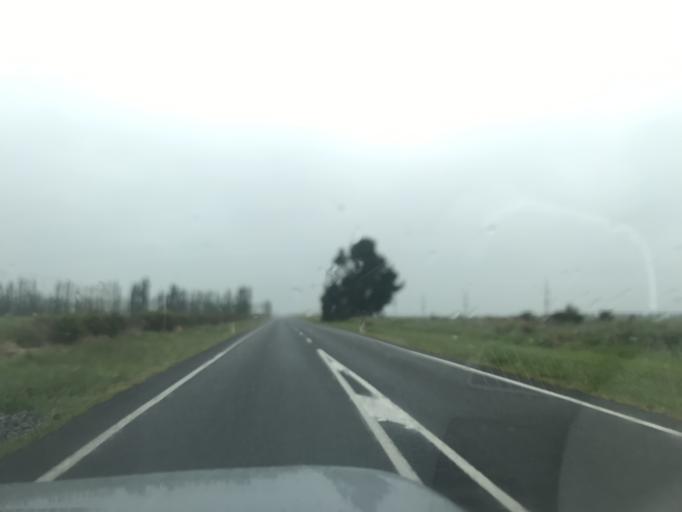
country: NZ
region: Canterbury
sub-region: Selwyn District
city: Darfield
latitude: -43.5027
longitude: 172.2198
